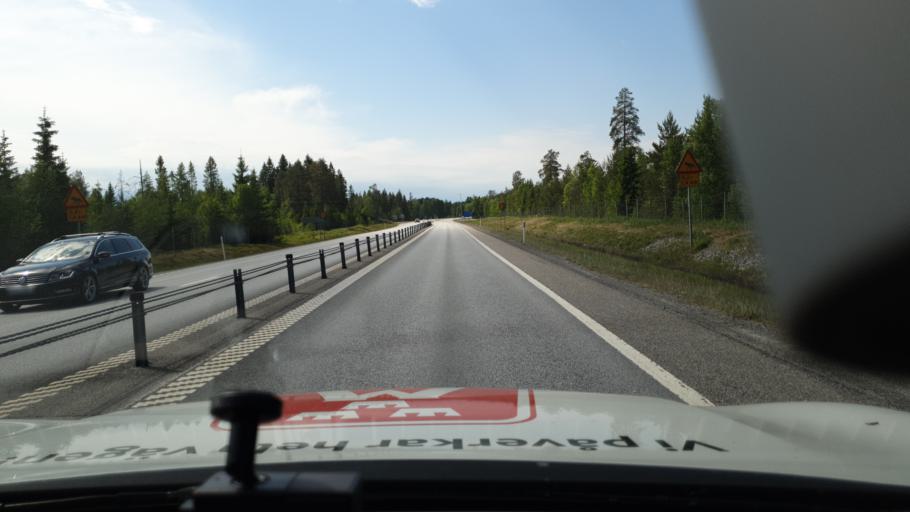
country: SE
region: Vaesterbotten
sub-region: Umea Kommun
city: Hoernefors
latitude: 63.6435
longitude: 19.9289
